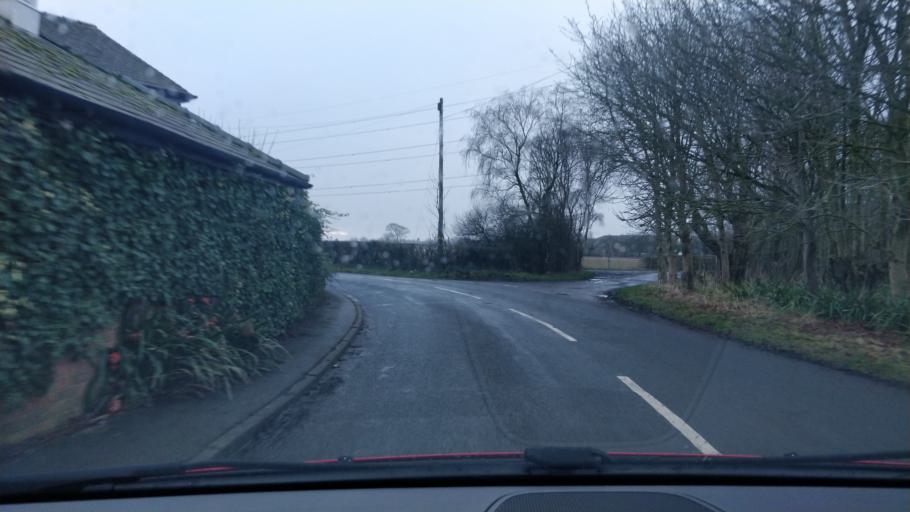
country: GB
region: England
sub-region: Lancashire
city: Tarleton
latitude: 53.6917
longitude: -2.8173
